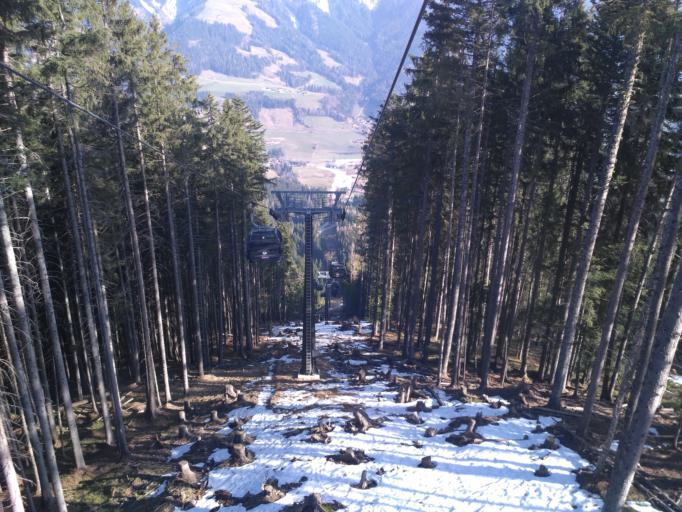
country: AT
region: Salzburg
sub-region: Politischer Bezirk Zell am See
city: Leogang
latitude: 47.4216
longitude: 12.7311
